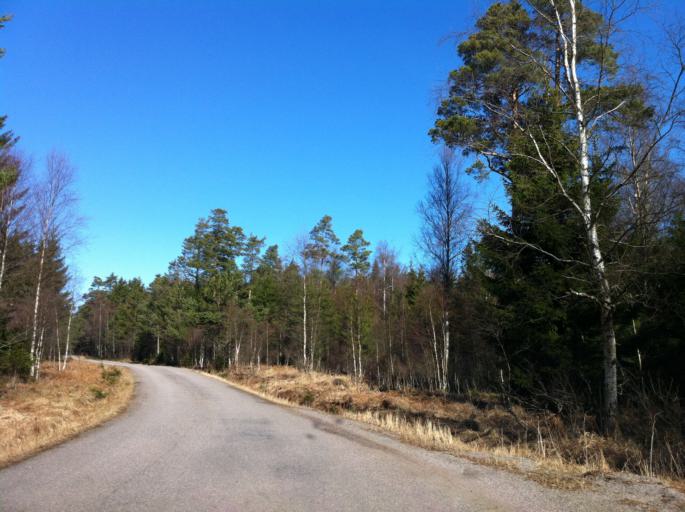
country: SE
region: Vaestra Goetaland
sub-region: Vanersborgs Kommun
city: Vargon
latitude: 58.3895
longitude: 12.4573
